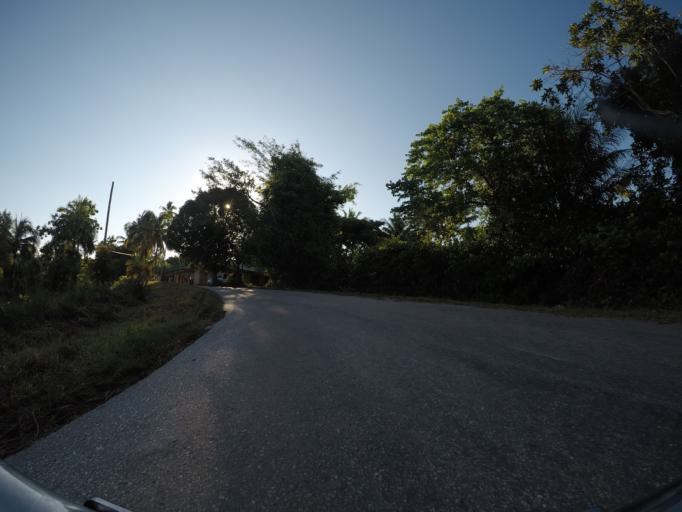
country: TZ
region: Pemba South
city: Mtambile
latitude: -5.3783
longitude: 39.6870
